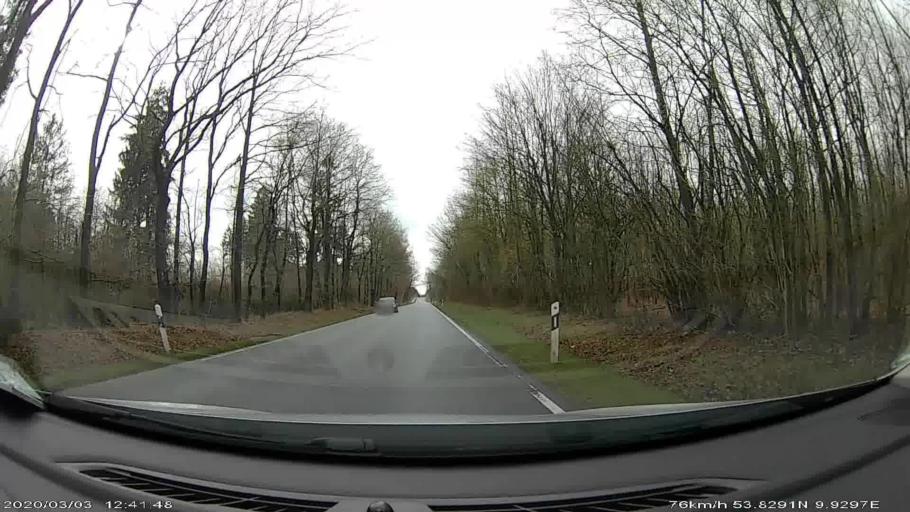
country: DE
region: Schleswig-Holstein
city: Kaltenkirchen
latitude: 53.8277
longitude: 9.9273
